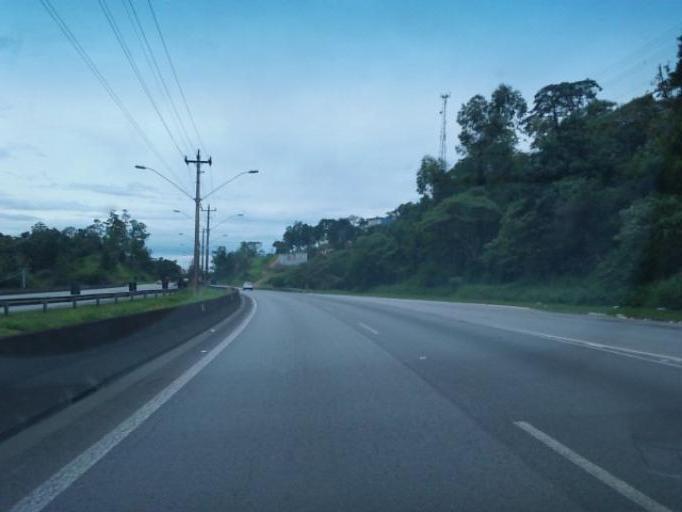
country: BR
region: Sao Paulo
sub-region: Sao Lourenco Da Serra
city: Sao Lourenco da Serra
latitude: -23.8601
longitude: -46.9461
